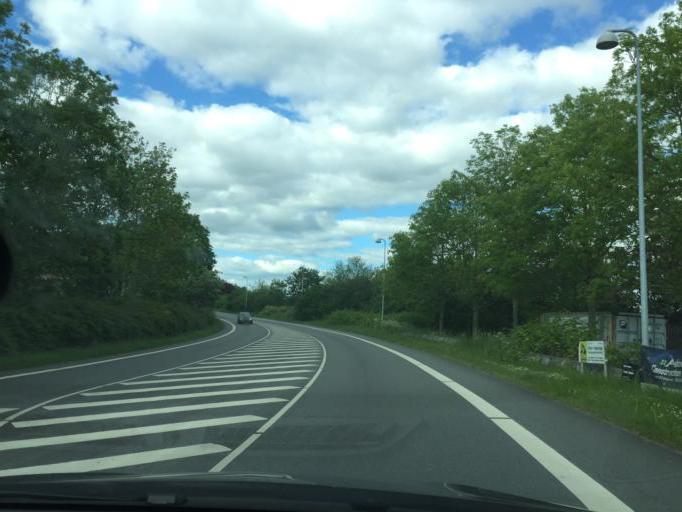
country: DK
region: South Denmark
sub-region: Odense Kommune
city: Bellinge
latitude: 55.3465
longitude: 10.3348
